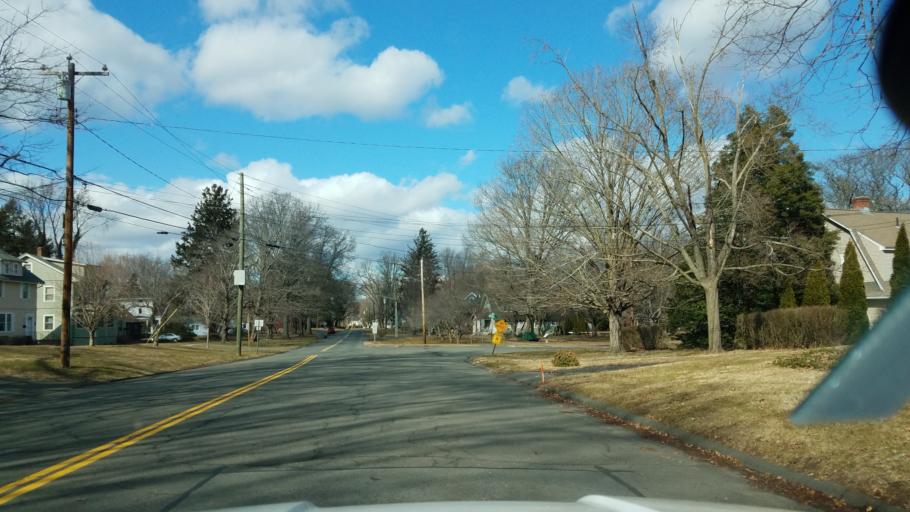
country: US
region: Connecticut
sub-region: Hartford County
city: Wethersfield
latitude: 41.7183
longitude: -72.6526
